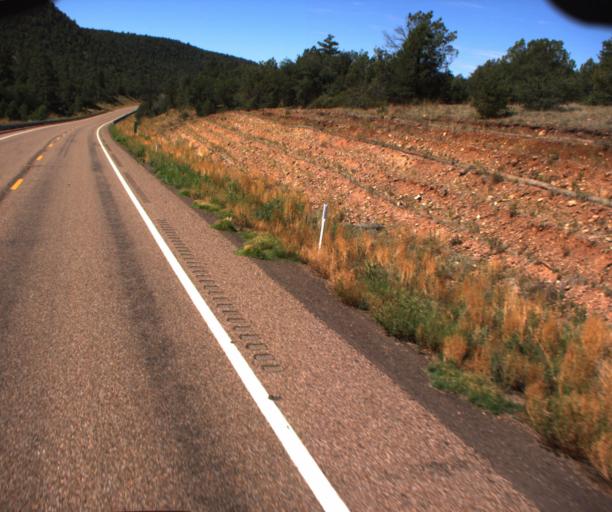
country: US
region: Arizona
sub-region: Navajo County
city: Cibecue
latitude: 33.9016
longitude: -110.3657
